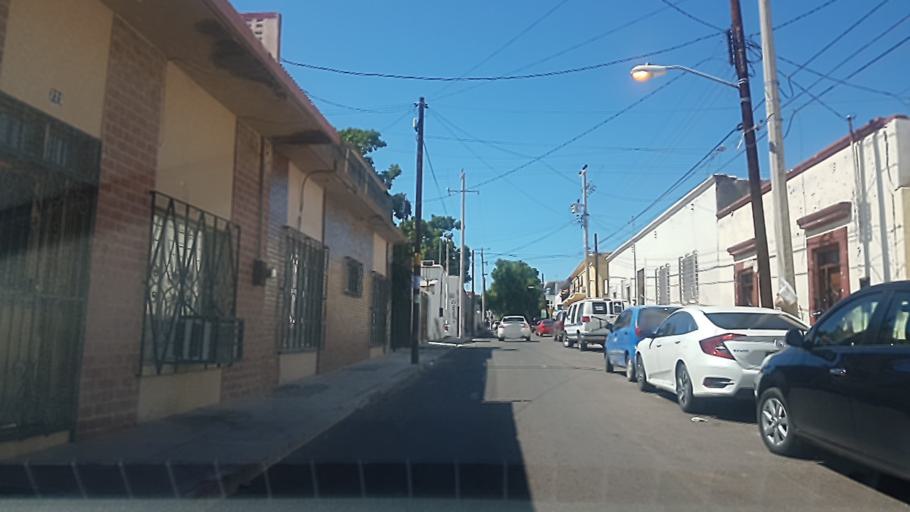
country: MX
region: Sonora
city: Heroica Guaymas
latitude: 27.9241
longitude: -110.8964
